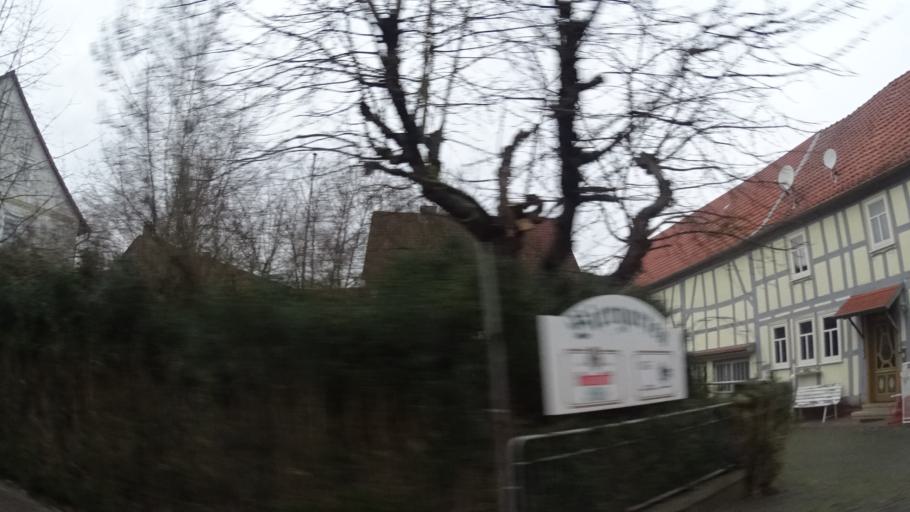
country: DE
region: Thuringia
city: Buttlar
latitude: 50.7564
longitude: 9.9532
